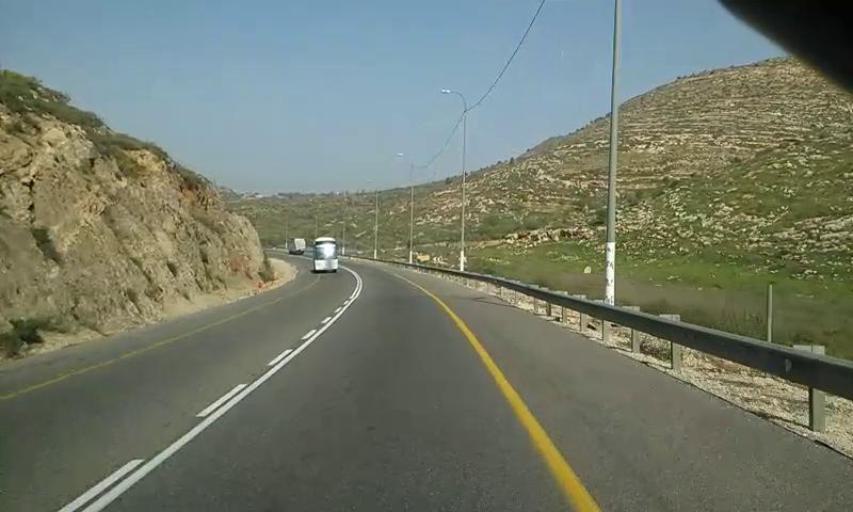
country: PS
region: West Bank
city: Qaryut
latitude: 32.0608
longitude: 35.2805
